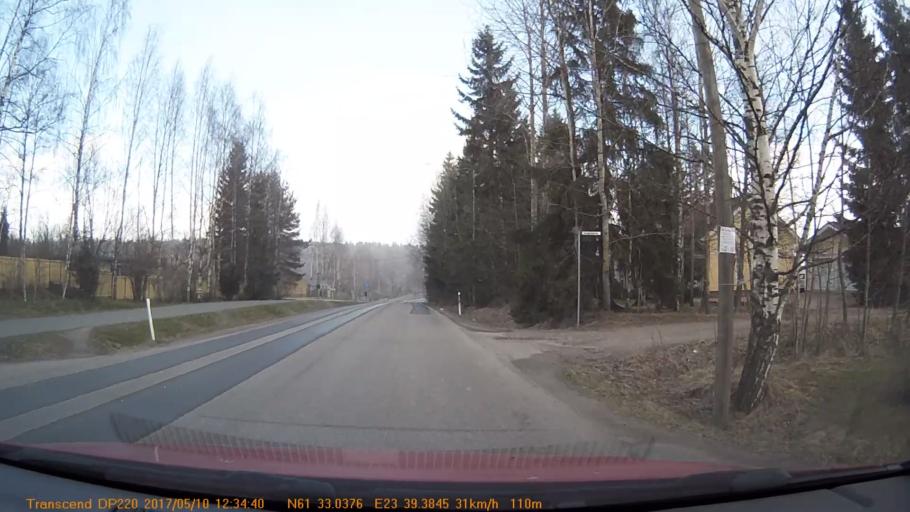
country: FI
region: Pirkanmaa
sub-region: Tampere
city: Yloejaervi
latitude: 61.5506
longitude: 23.6566
